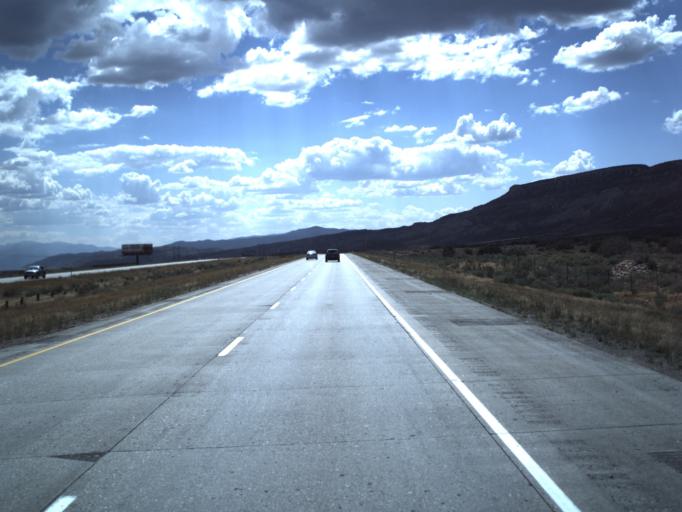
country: US
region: Utah
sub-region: Sevier County
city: Aurora
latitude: 38.8540
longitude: -111.9965
